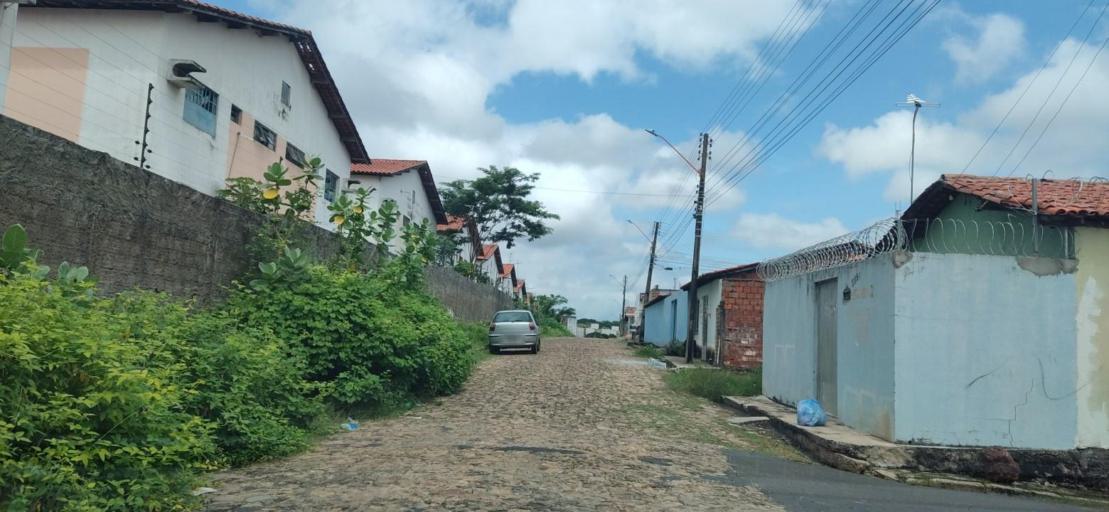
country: BR
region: Piaui
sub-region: Teresina
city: Teresina
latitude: -5.0673
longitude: -42.7520
